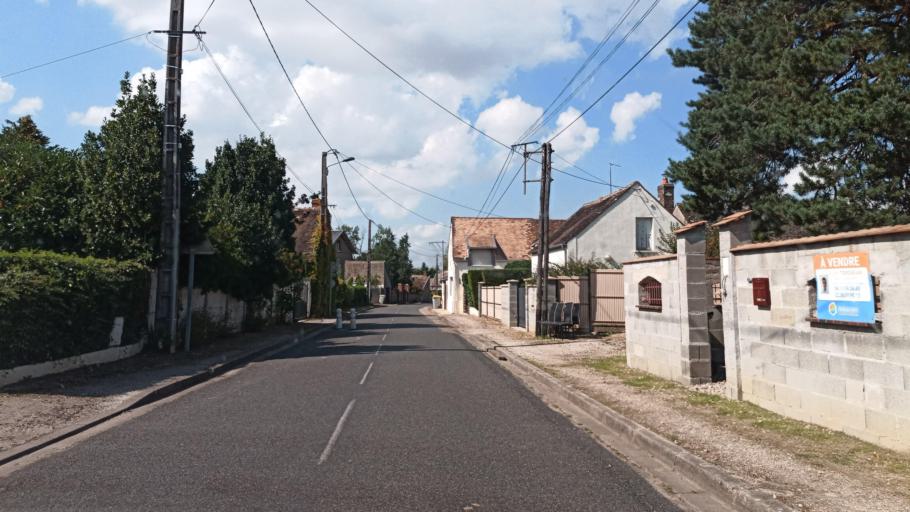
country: FR
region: Bourgogne
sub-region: Departement de l'Yonne
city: Saint-Valerien
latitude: 48.1469
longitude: 3.0900
